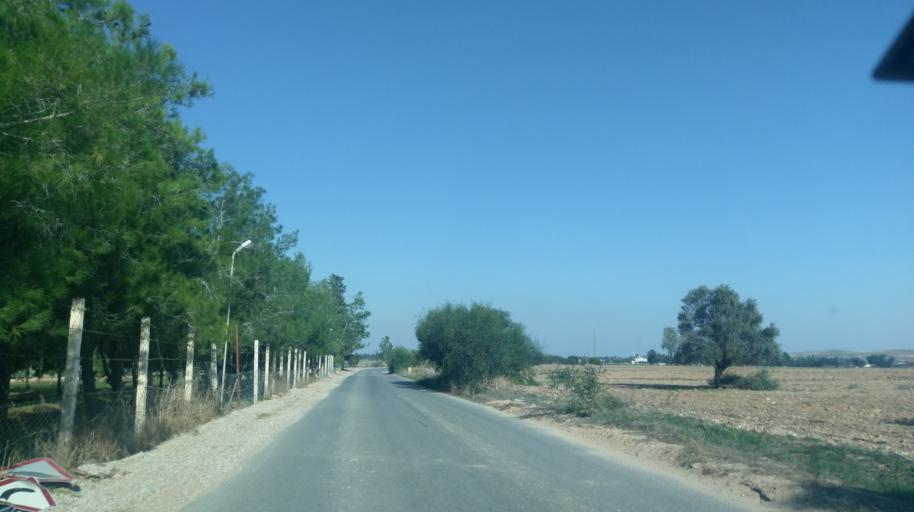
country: CY
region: Larnaka
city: Troulloi
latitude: 35.0850
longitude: 33.6148
